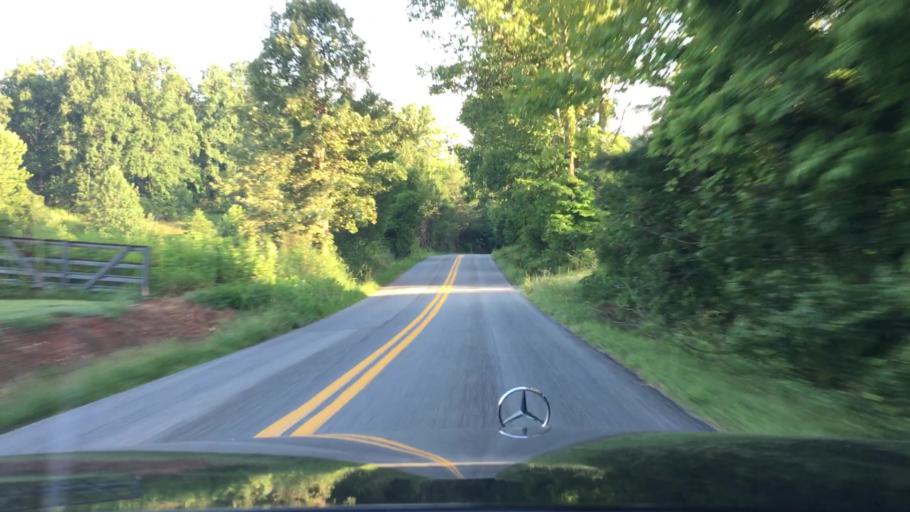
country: US
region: Virginia
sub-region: Campbell County
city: Timberlake
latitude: 37.2761
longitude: -79.2680
